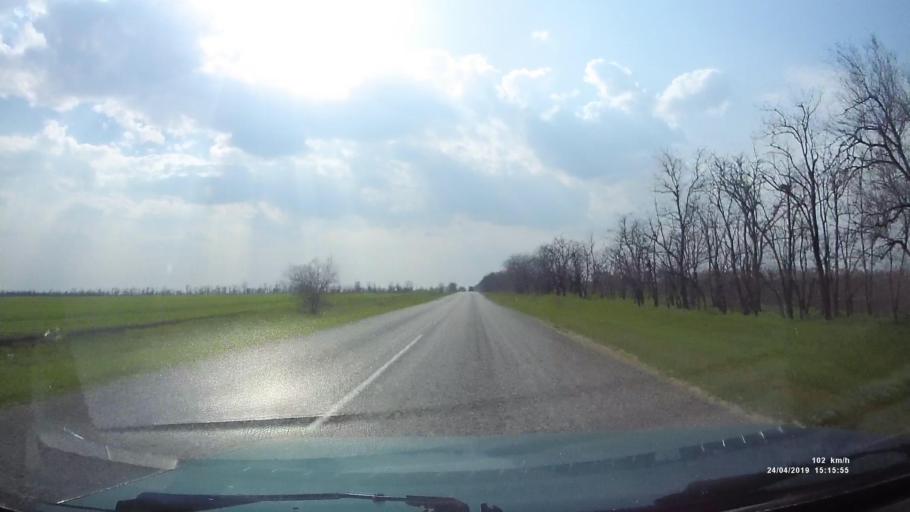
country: RU
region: Rostov
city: Remontnoye
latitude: 46.5465
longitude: 43.2244
